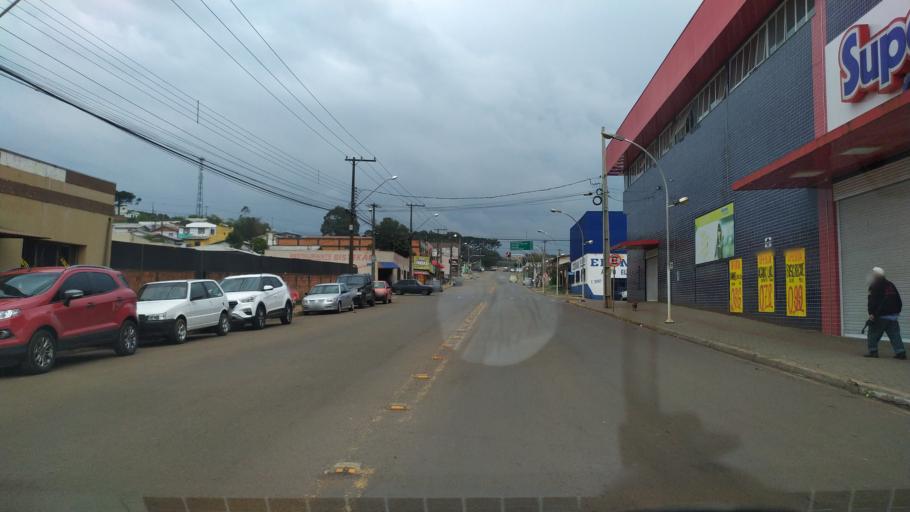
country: BR
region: Parana
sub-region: Palmas
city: Palmas
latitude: -26.4898
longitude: -51.9984
